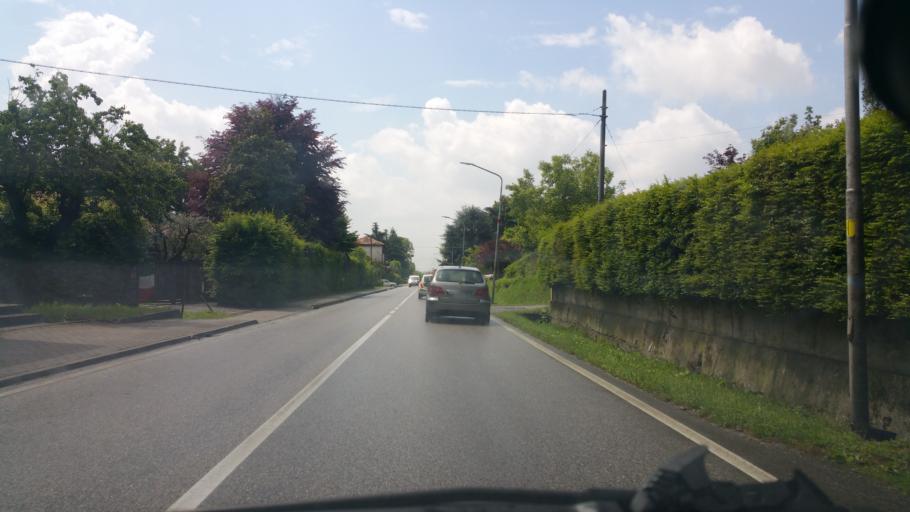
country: IT
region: Veneto
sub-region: Provincia di Treviso
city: Nervesa della Battaglia
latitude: 45.8233
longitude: 12.2036
